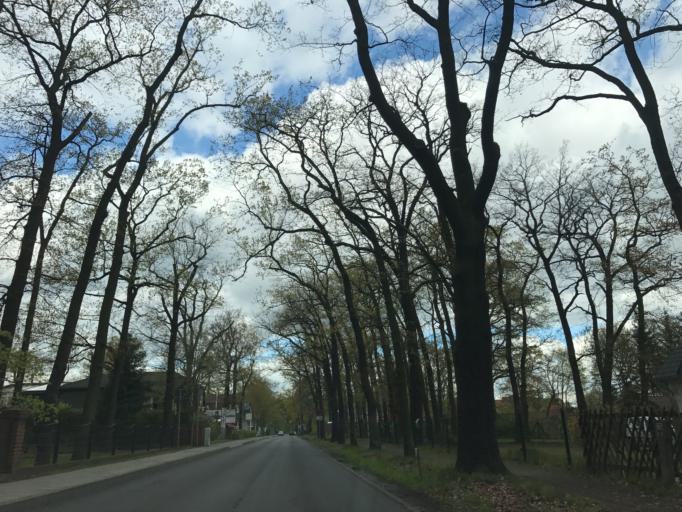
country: DE
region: Brandenburg
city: Brieselang
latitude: 52.5790
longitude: 13.0028
